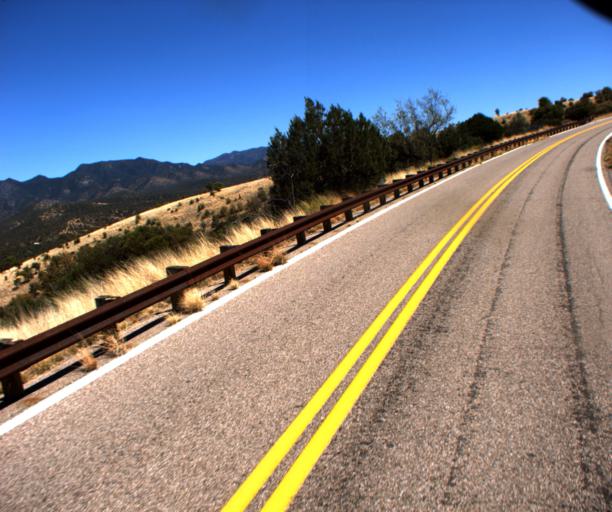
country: US
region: Arizona
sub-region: Cochise County
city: Sierra Vista
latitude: 31.4937
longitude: -110.4909
